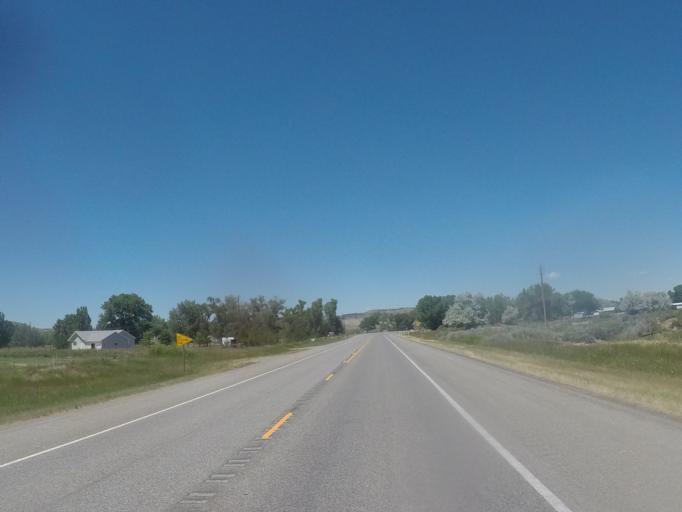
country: US
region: Montana
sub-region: Carbon County
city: Red Lodge
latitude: 45.3330
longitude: -108.9153
